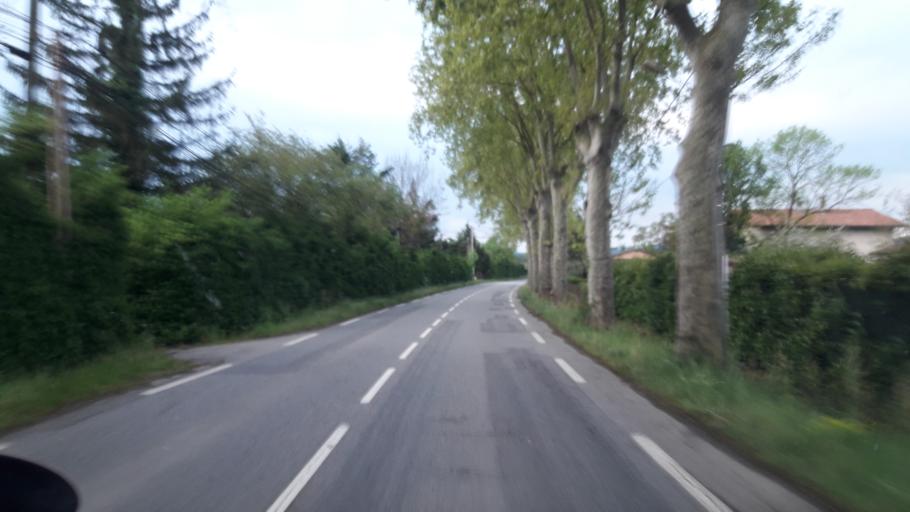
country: FR
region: Midi-Pyrenees
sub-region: Departement de la Haute-Garonne
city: Cazeres
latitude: 43.2248
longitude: 1.0845
